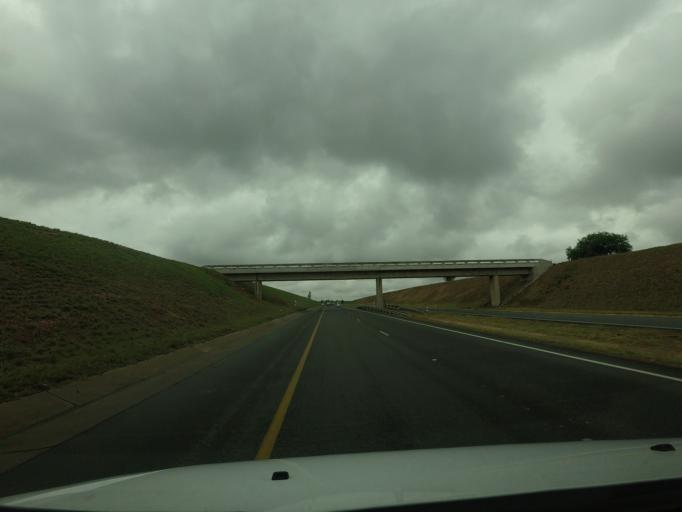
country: ZA
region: Mpumalanga
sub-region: Nkangala District Municipality
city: Middelburg
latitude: -25.8307
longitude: 29.4944
